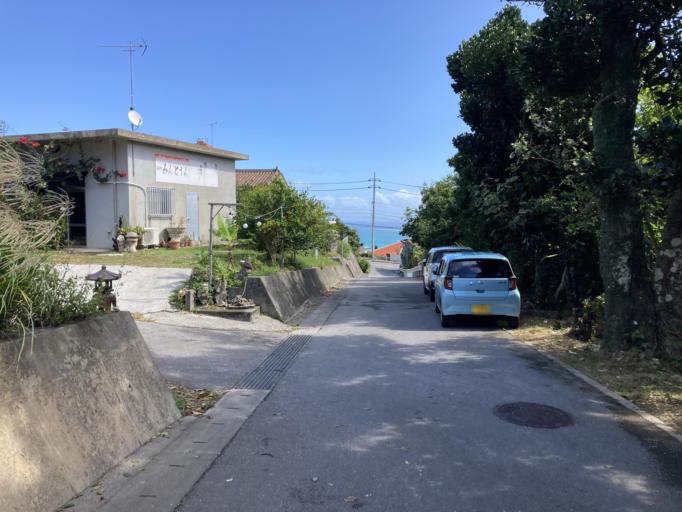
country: JP
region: Okinawa
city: Tomigusuku
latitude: 26.1449
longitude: 127.7916
